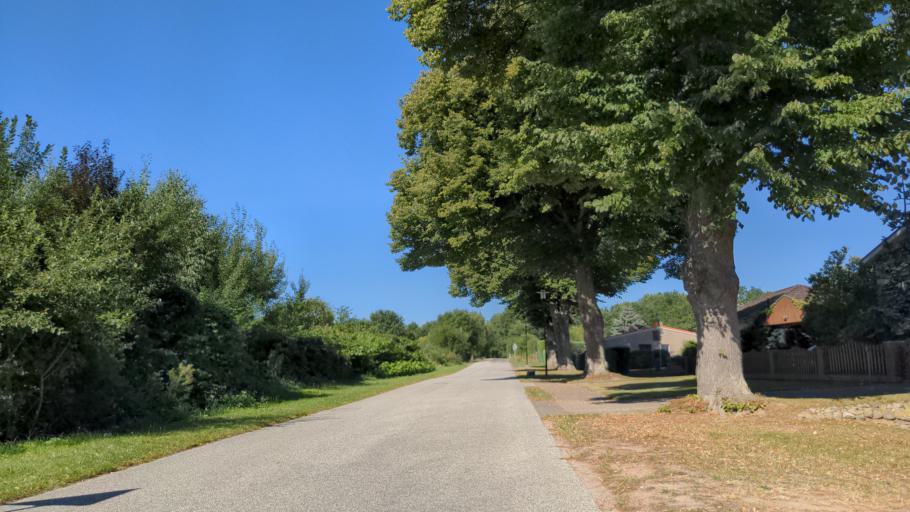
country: DE
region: Mecklenburg-Vorpommern
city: Selmsdorf
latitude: 53.8483
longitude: 10.9130
